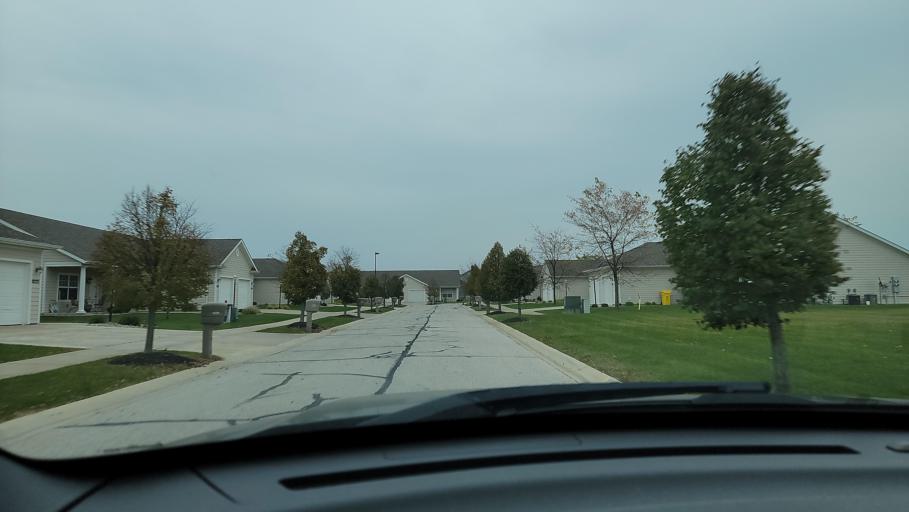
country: US
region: Indiana
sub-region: Porter County
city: Portage
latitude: 41.5436
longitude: -87.1733
